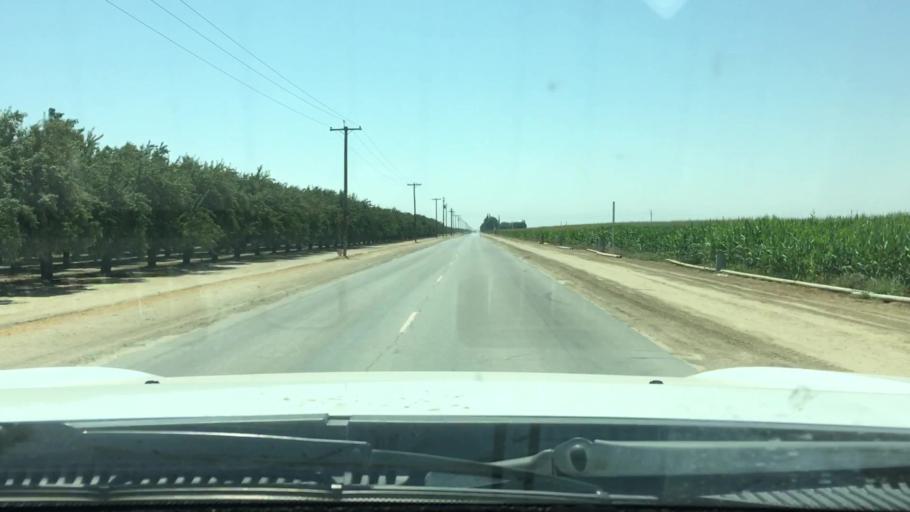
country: US
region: California
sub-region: Kern County
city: Wasco
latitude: 35.6709
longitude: -119.4375
